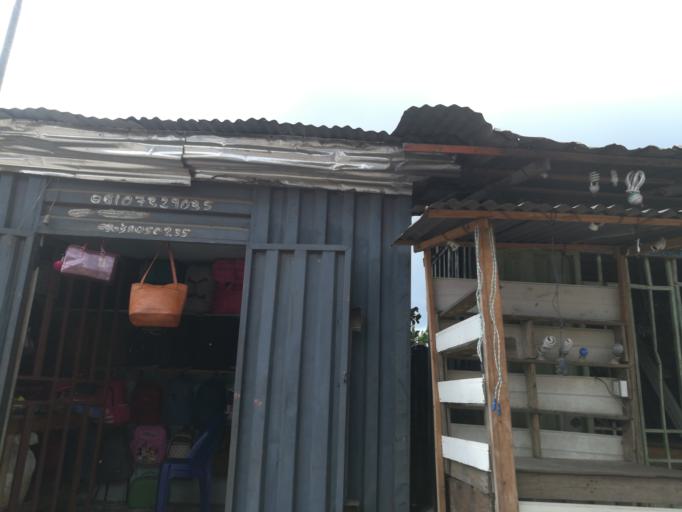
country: NG
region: Rivers
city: Okrika
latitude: 4.7293
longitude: 7.1477
